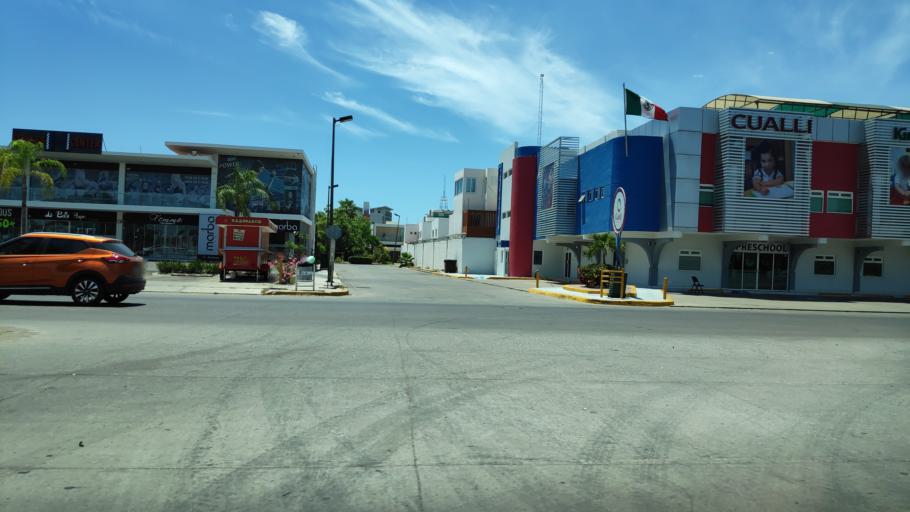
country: MX
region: Sinaloa
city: Culiacan
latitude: 24.8259
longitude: -107.3998
